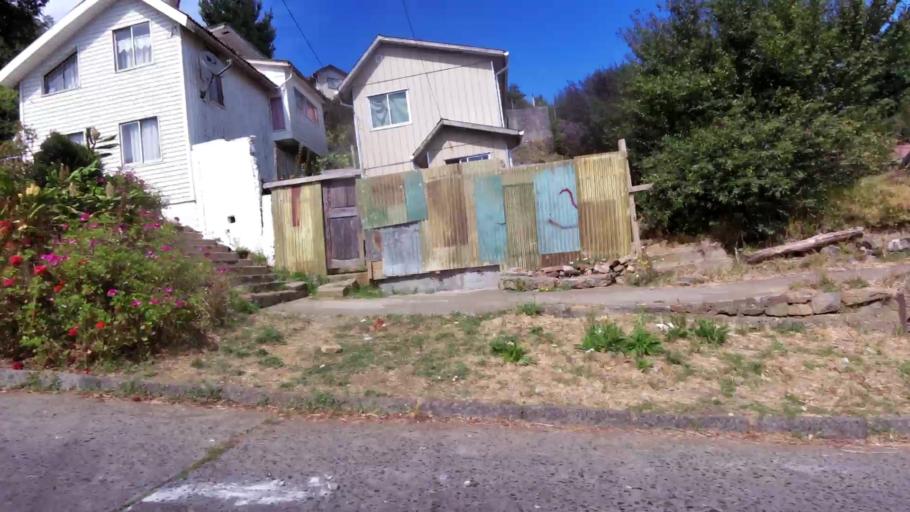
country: CL
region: Biobio
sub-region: Provincia de Concepcion
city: Talcahuano
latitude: -36.7159
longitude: -73.1162
